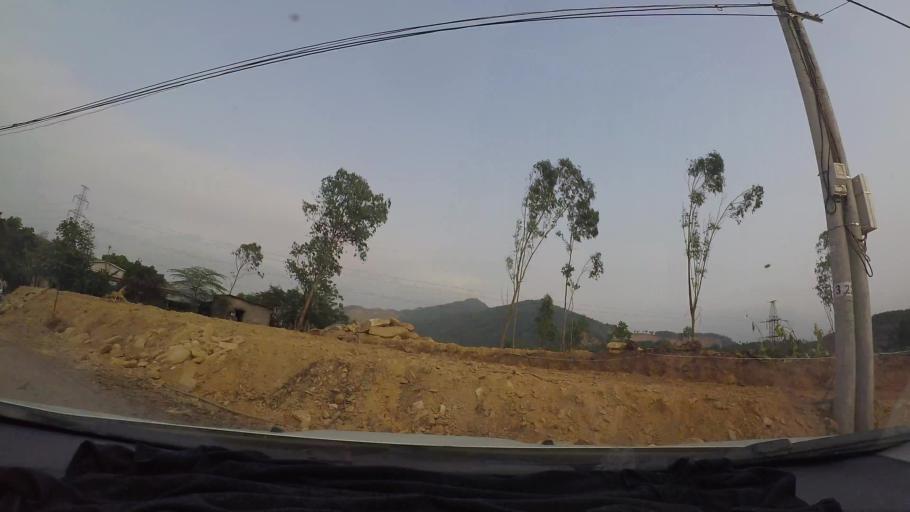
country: VN
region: Da Nang
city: Lien Chieu
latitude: 16.0543
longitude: 108.1074
